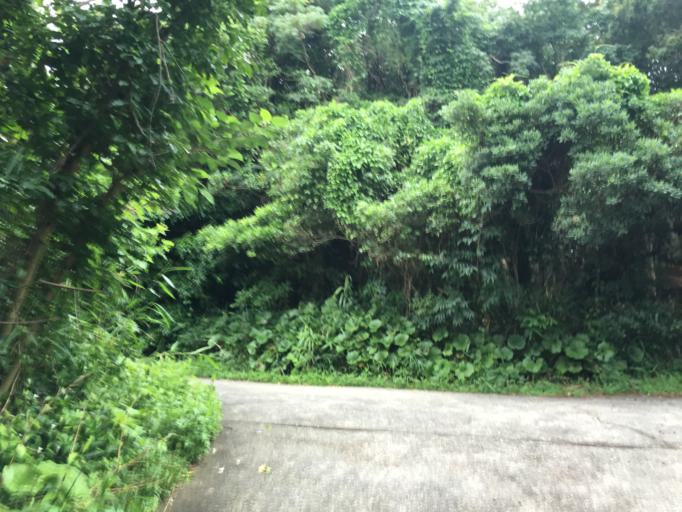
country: JP
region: Aichi
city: Ishiki
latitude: 34.7287
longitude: 137.0469
